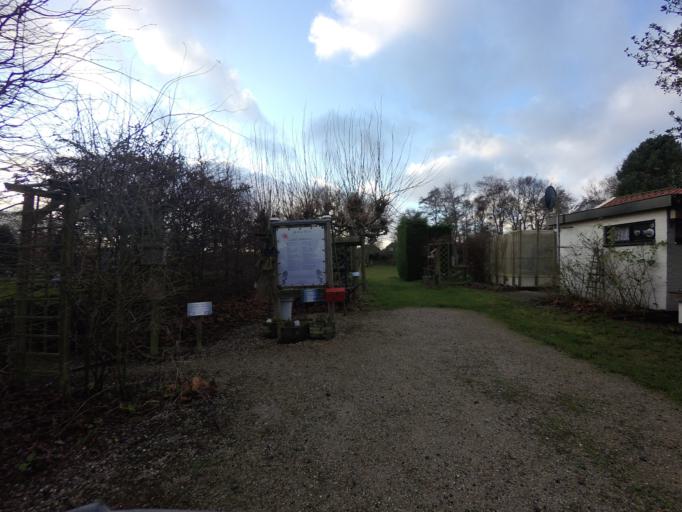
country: NL
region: North Holland
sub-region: Gemeente Texel
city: Den Burg
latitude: 53.0933
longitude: 4.7756
